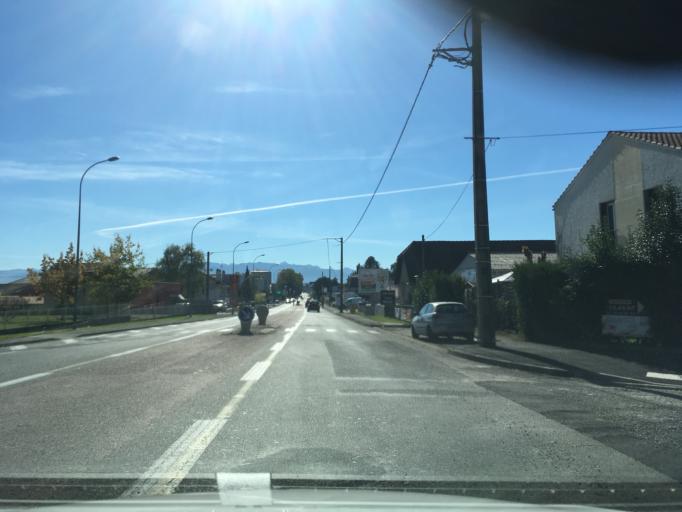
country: FR
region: Aquitaine
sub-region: Departement des Pyrenees-Atlantiques
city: Lons
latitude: 43.3345
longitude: -0.3798
